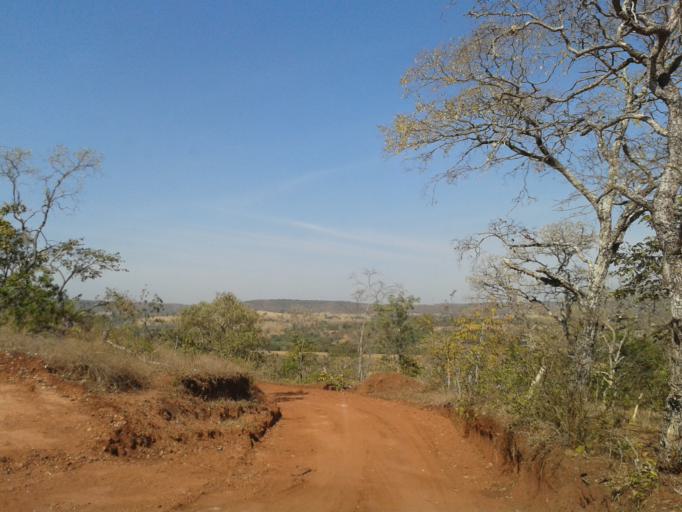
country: BR
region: Minas Gerais
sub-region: Santa Vitoria
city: Santa Vitoria
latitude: -19.2294
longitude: -50.0410
